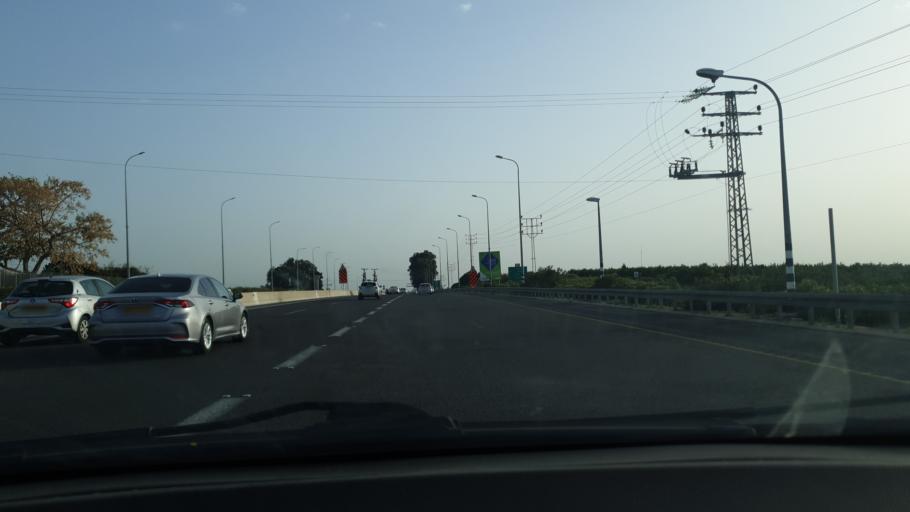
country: IL
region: Central District
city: Even Yehuda
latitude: 32.2494
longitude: 34.8894
